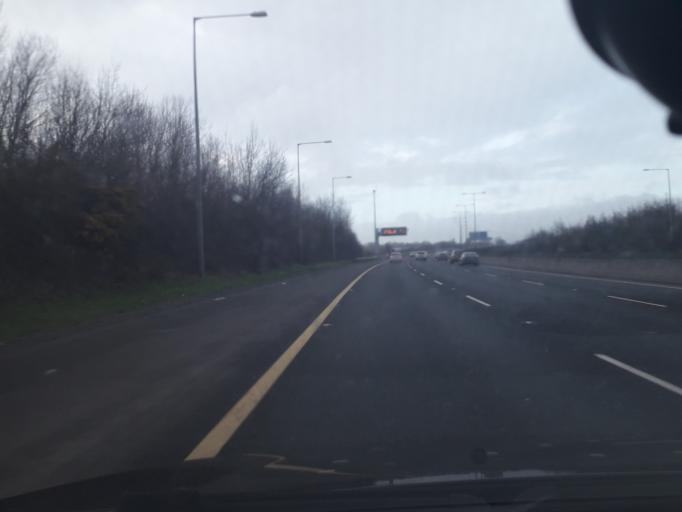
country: IE
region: Leinster
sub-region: Fingal County
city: Swords
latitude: 53.4582
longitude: -6.2043
